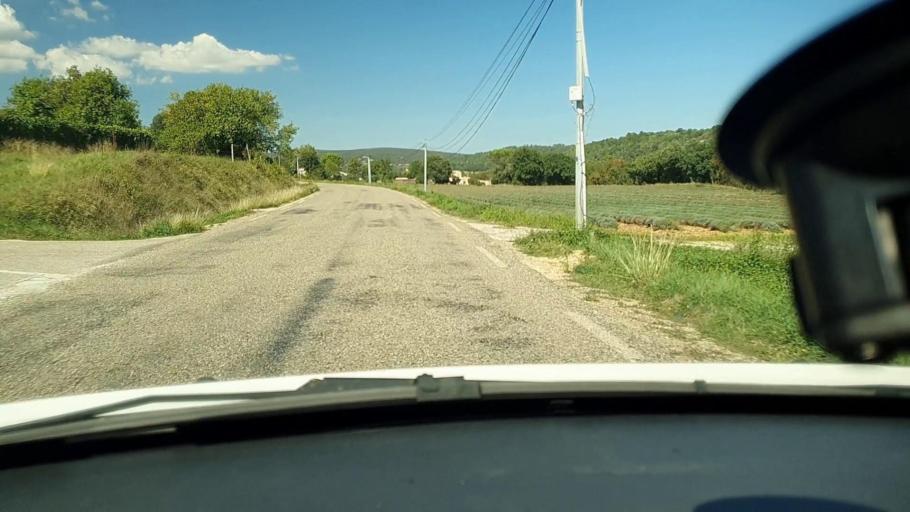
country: FR
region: Languedoc-Roussillon
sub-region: Departement du Gard
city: Goudargues
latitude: 44.1608
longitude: 4.4582
